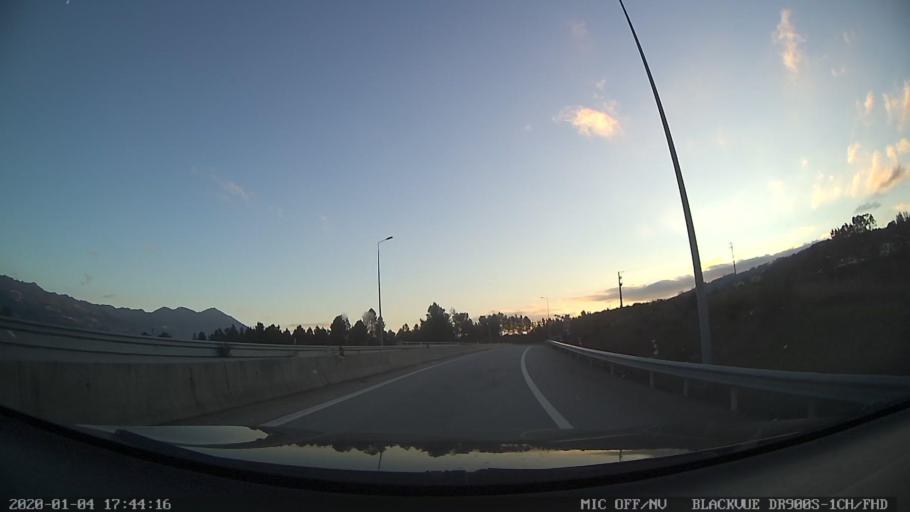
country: PT
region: Braga
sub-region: Cabeceiras de Basto
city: Cabeceiras de Basto
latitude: 41.4740
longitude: -7.9469
